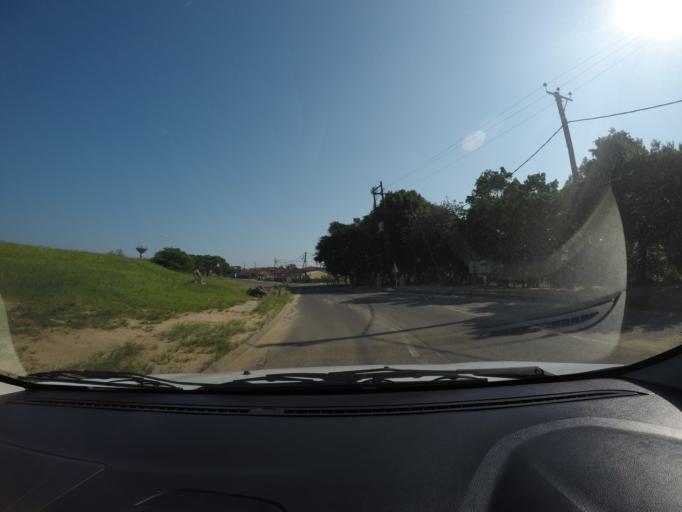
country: ZA
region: KwaZulu-Natal
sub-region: uThungulu District Municipality
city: Richards Bay
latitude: -28.7194
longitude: 32.0396
